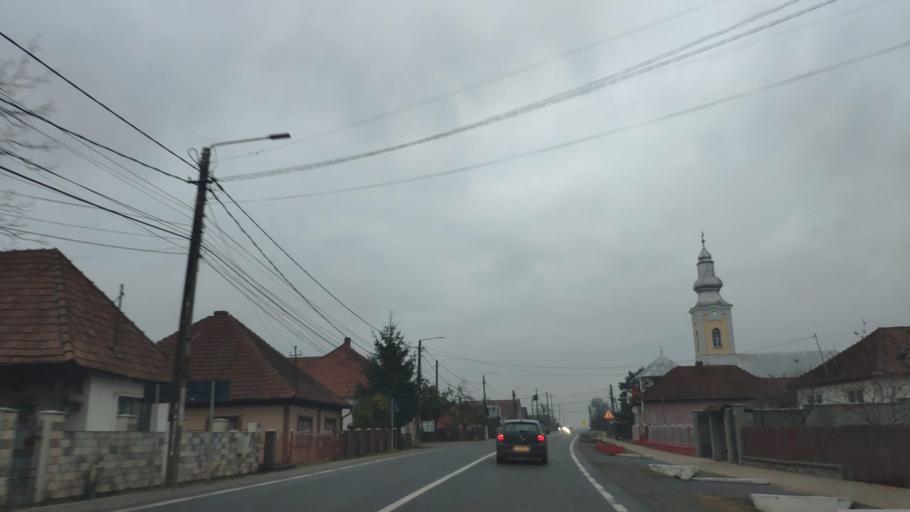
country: RO
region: Maramures
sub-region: Comuna Cicarlau
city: Ilba
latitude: 47.7127
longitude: 23.3539
